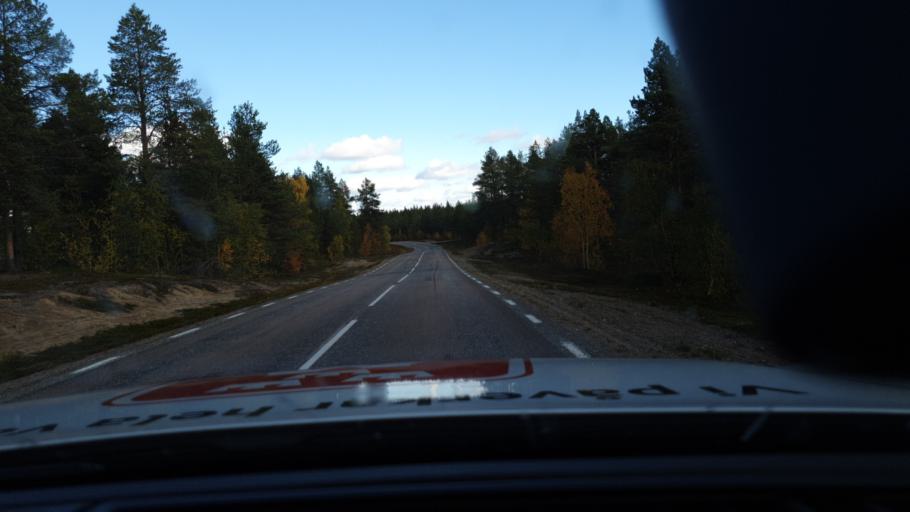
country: NO
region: Finnmark Fylke
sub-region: Kautokeino
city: Kautokeino
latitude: 68.3609
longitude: 22.7748
